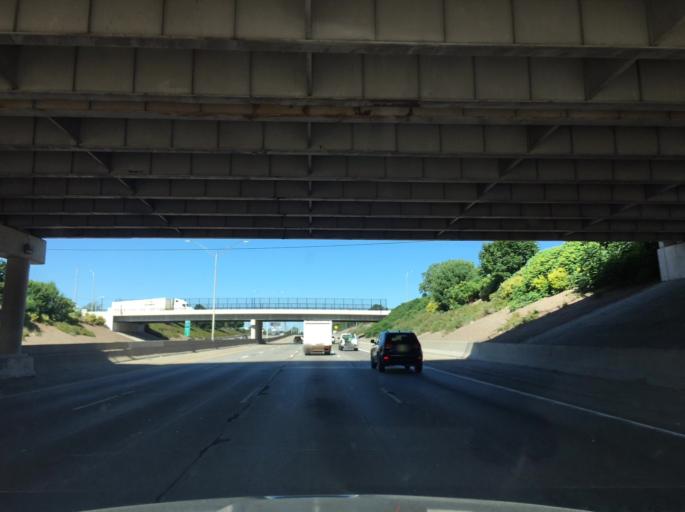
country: US
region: Michigan
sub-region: Macomb County
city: Center Line
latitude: 42.4918
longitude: -83.0276
